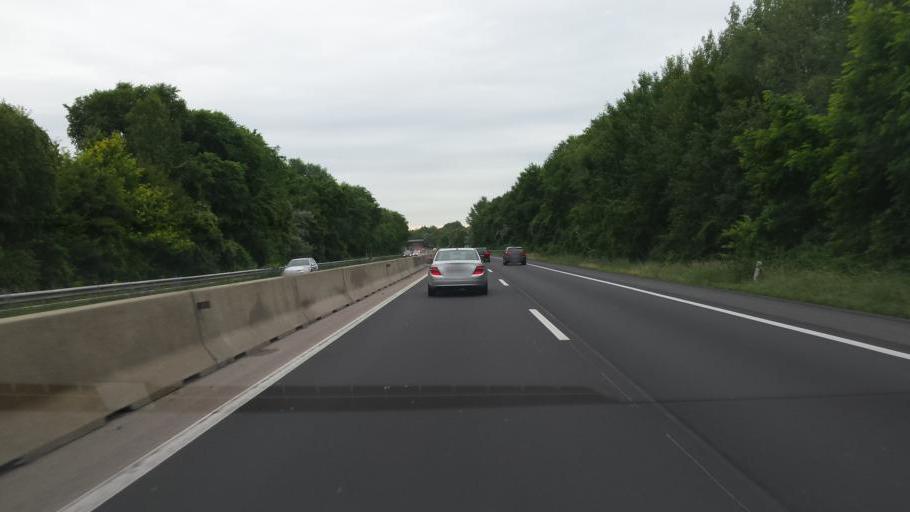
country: AT
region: Lower Austria
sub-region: Politischer Bezirk Bruck an der Leitha
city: Bruck an der Leitha
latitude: 48.0618
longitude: 16.7015
